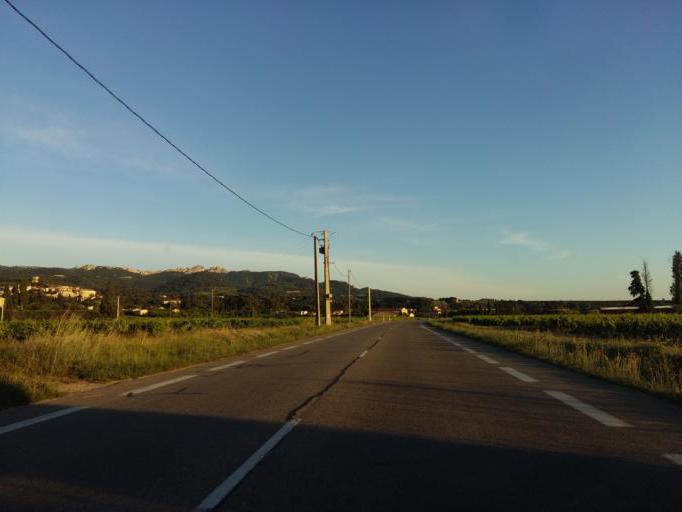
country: FR
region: Provence-Alpes-Cote d'Azur
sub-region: Departement du Vaucluse
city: Sablet
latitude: 44.1992
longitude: 4.9991
